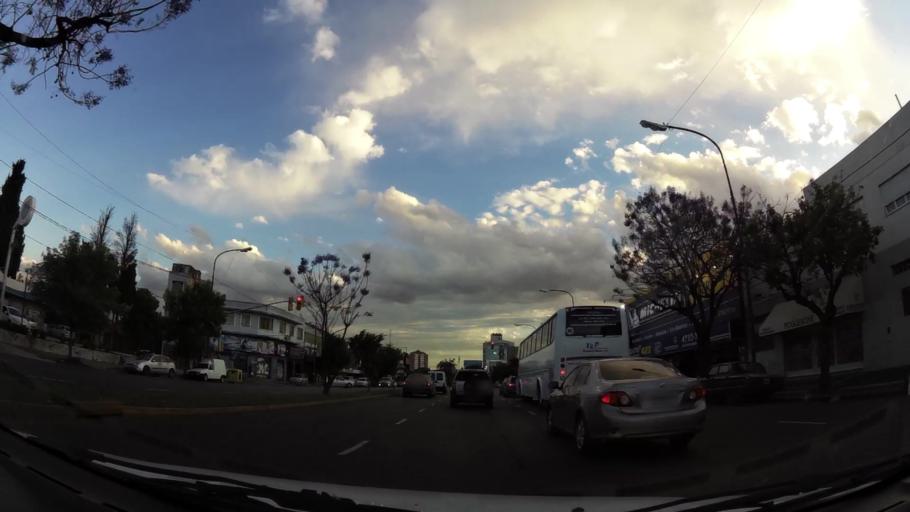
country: AR
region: Buenos Aires
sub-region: Partido de Vicente Lopez
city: Olivos
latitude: -34.4957
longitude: -58.4980
